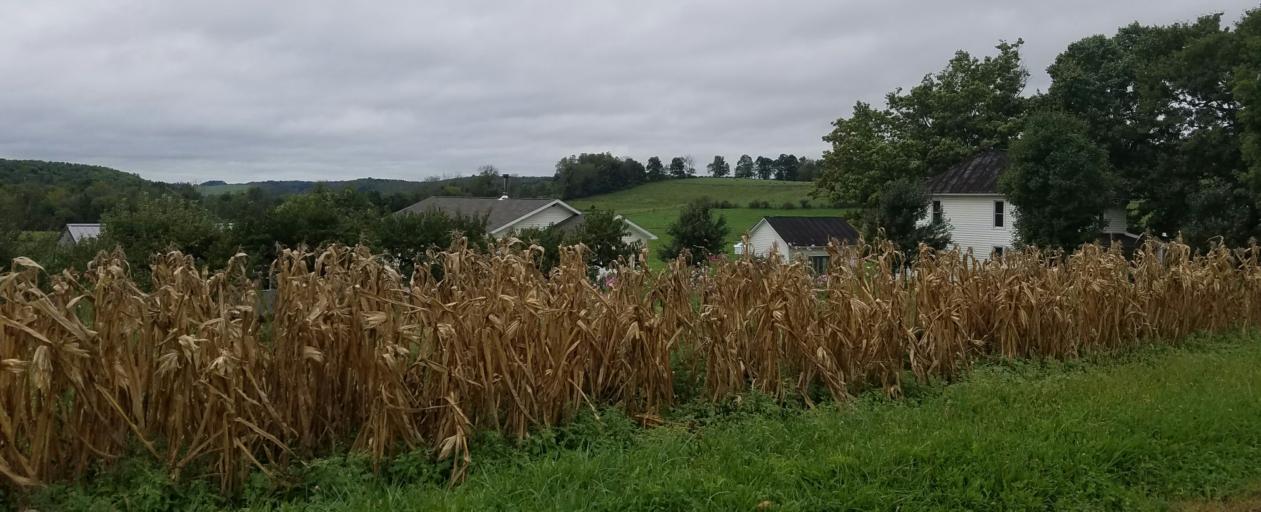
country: US
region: Ohio
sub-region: Ashland County
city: Loudonville
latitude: 40.5558
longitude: -82.2943
